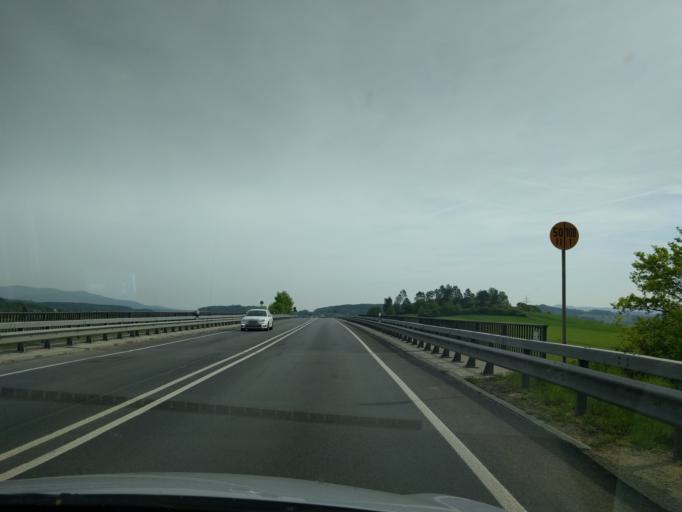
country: DE
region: Bavaria
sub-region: Upper Palatinate
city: Chamerau
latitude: 49.2185
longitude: 12.7156
